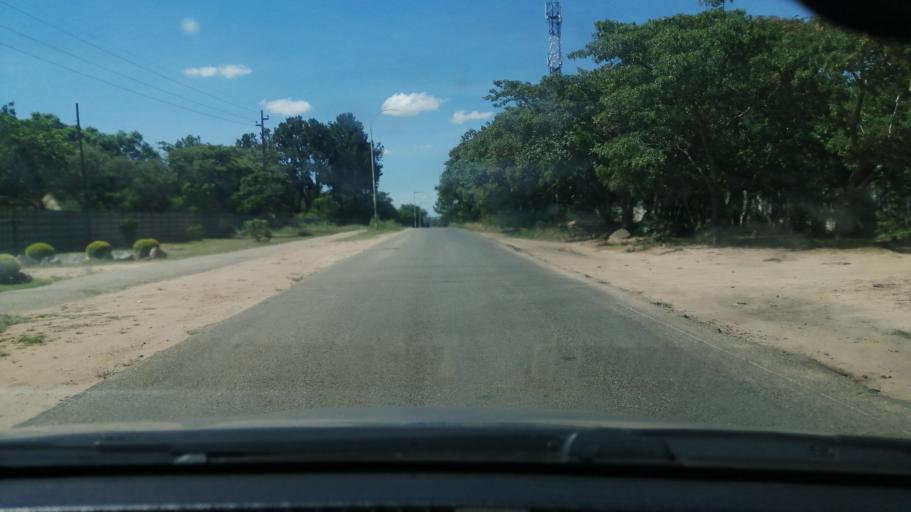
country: ZW
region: Harare
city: Epworth
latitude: -17.8257
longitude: 31.1256
